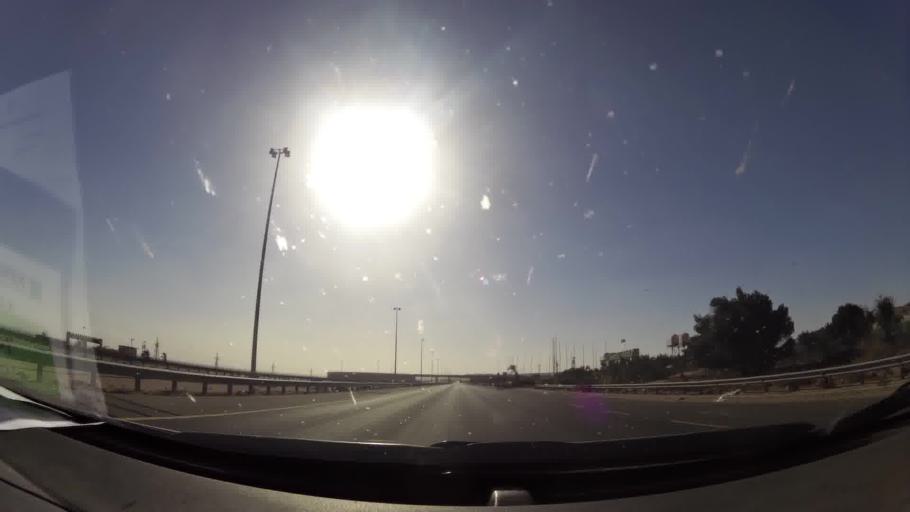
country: KW
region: Al Asimah
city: Kuwait City
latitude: 29.5255
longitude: 47.8185
